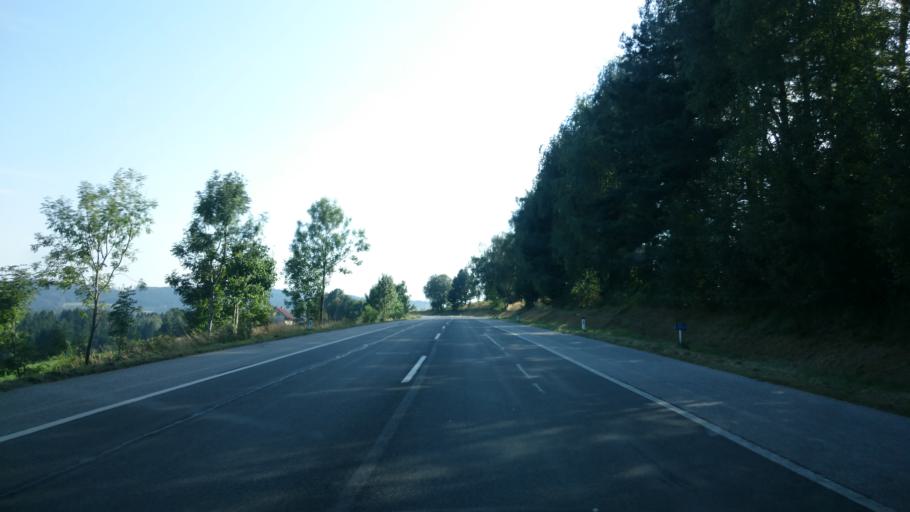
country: AT
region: Lower Austria
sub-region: Politischer Bezirk Neunkirchen
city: Monichkirchen
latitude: 47.5364
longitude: 16.0733
